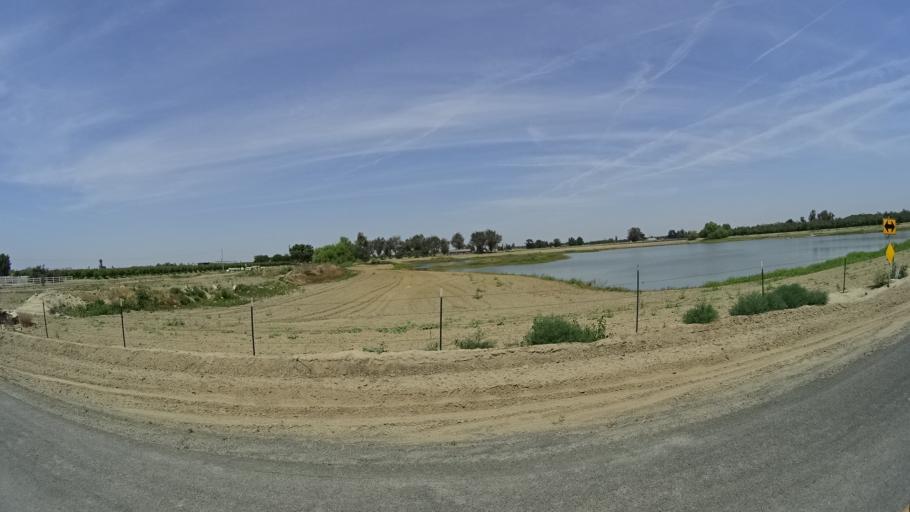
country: US
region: California
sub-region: Fresno County
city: Riverdale
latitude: 36.3948
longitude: -119.8153
